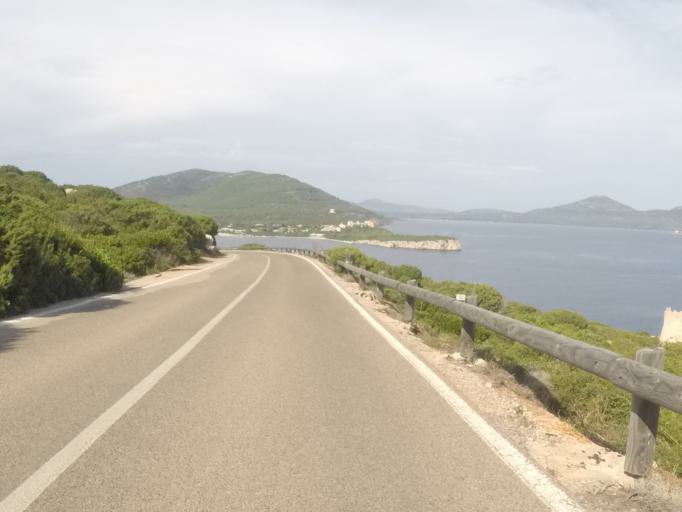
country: IT
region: Sardinia
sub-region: Provincia di Sassari
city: Alghero
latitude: 40.5710
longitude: 8.1628
